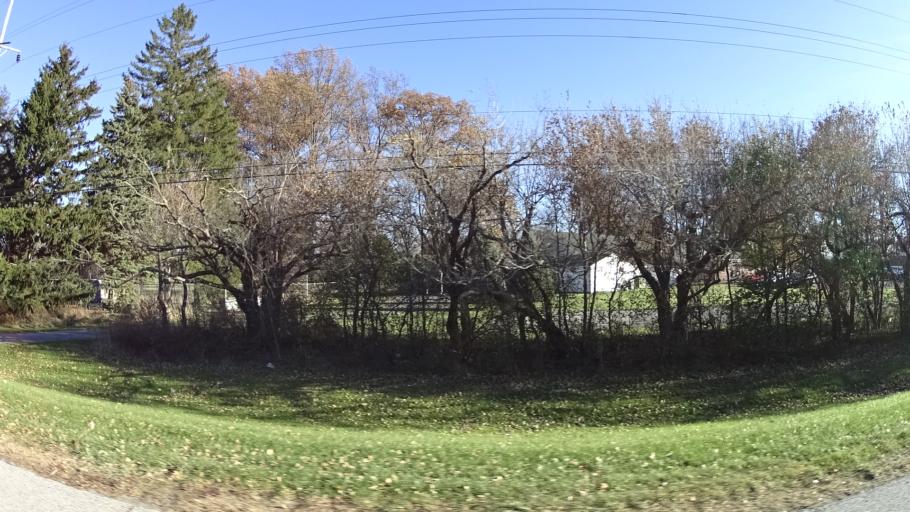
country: US
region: Ohio
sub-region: Lorain County
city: Elyria
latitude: 41.3305
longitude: -82.1292
